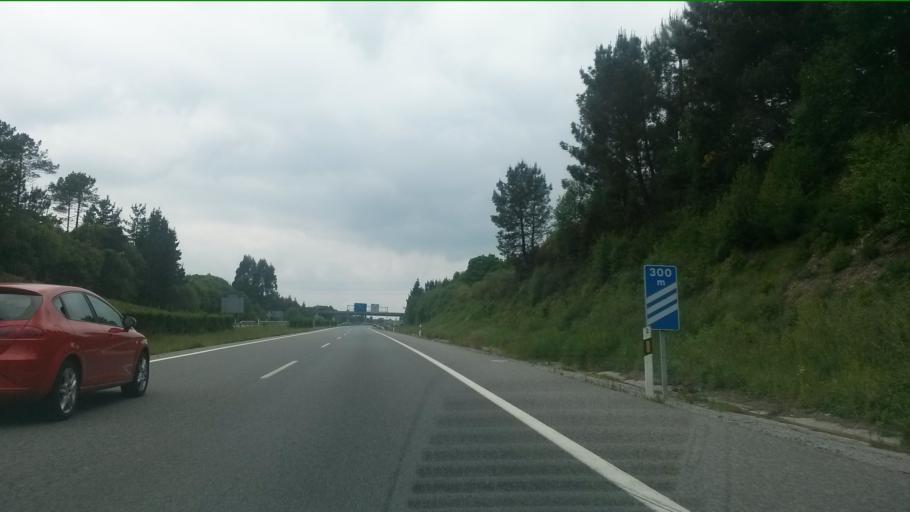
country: ES
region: Galicia
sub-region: Provincia de Lugo
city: Guitiriz
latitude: 43.1920
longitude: -7.9430
